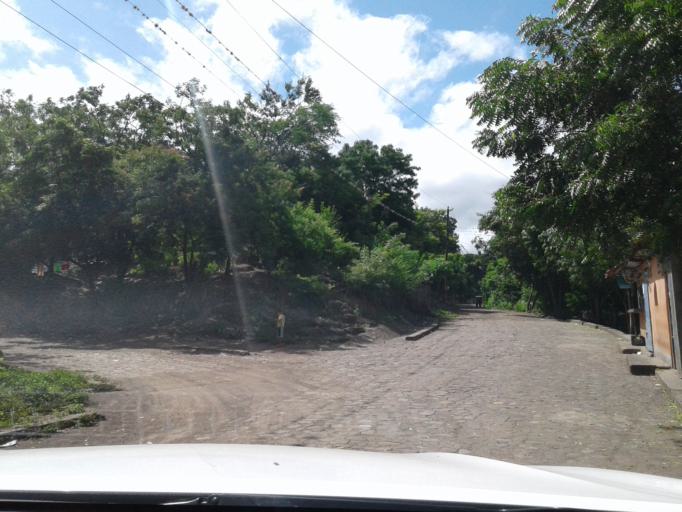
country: NI
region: Matagalpa
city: Terrabona
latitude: 12.8433
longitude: -86.0276
